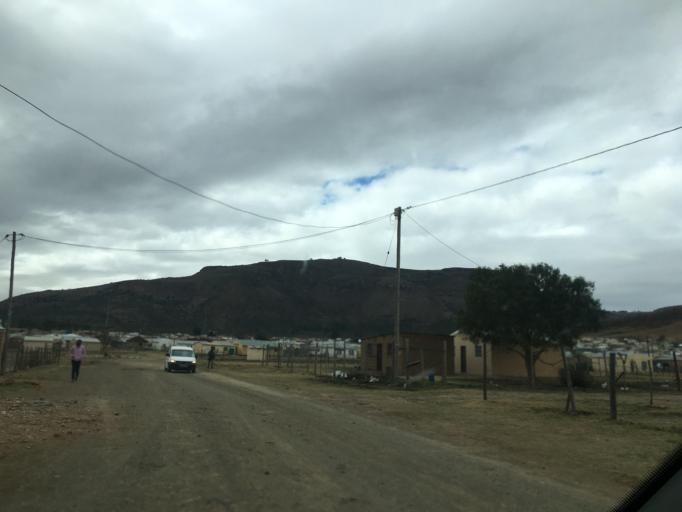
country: ZA
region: Eastern Cape
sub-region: Chris Hani District Municipality
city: Cala
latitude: -31.5369
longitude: 27.6990
